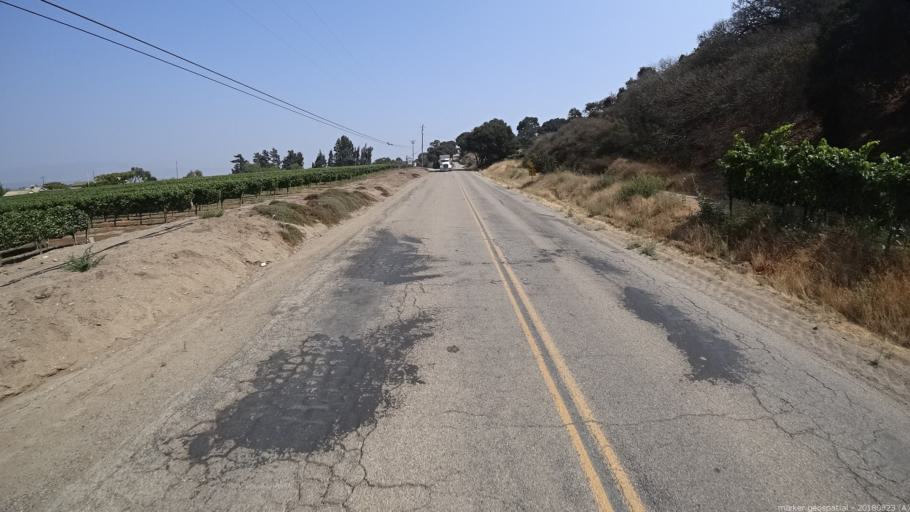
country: US
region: California
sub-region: Monterey County
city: Gonzales
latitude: 36.4718
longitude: -121.4694
